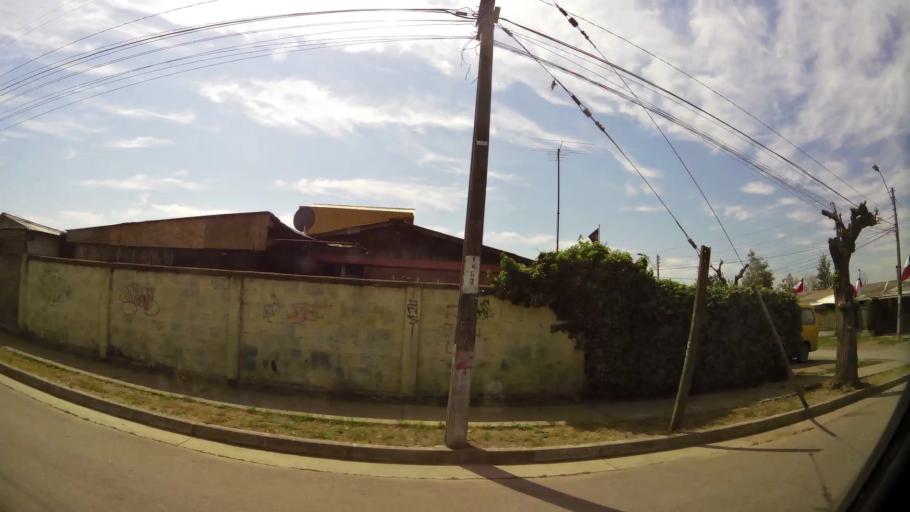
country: CL
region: Santiago Metropolitan
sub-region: Provincia de Talagante
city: Talagante
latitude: -33.6640
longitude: -70.9203
